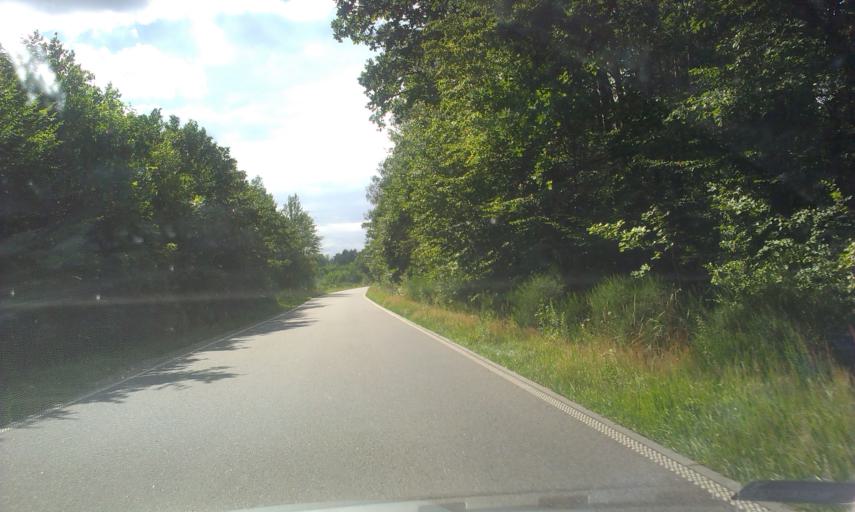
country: PL
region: Masovian Voivodeship
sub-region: Powiat zyrardowski
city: Radziejowice
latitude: 51.9675
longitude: 20.5930
